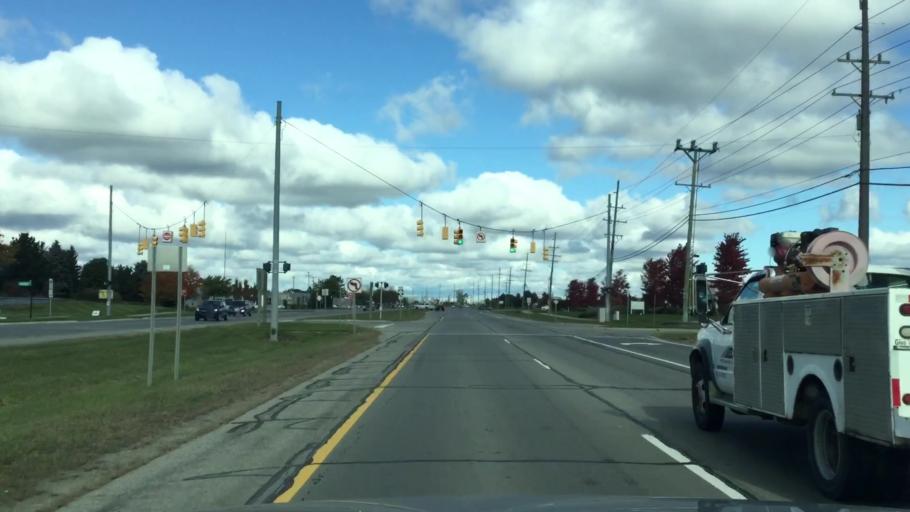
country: US
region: Michigan
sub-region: Oakland County
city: Oxford
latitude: 42.8355
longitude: -83.2716
